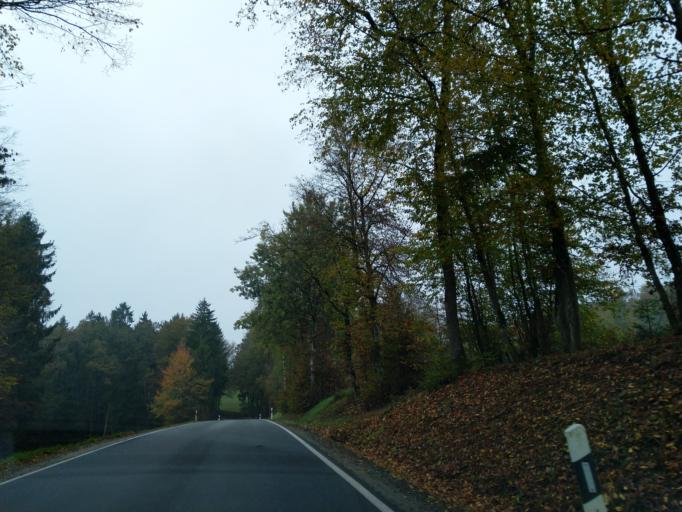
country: DE
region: Bavaria
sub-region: Lower Bavaria
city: Auerbach
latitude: 48.7904
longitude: 13.1077
